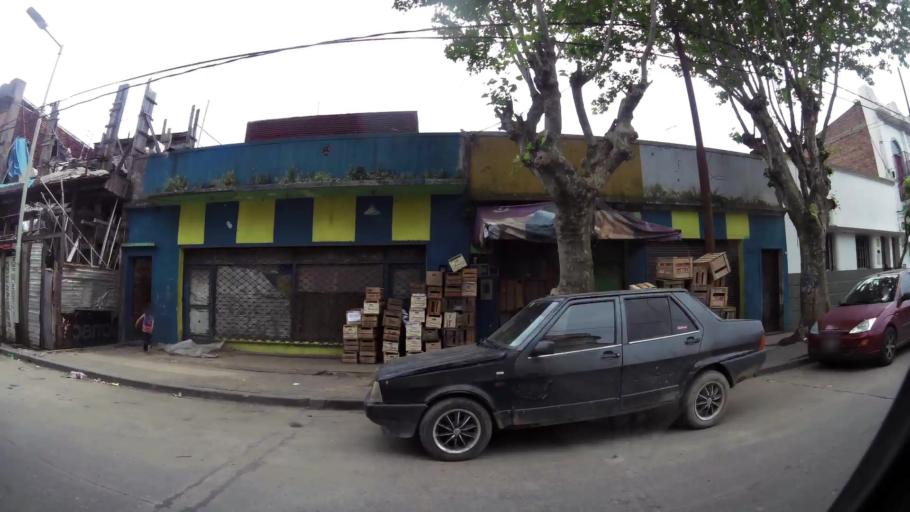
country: AR
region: Buenos Aires
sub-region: Partido de Avellaneda
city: Avellaneda
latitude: -34.6554
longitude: -58.3441
